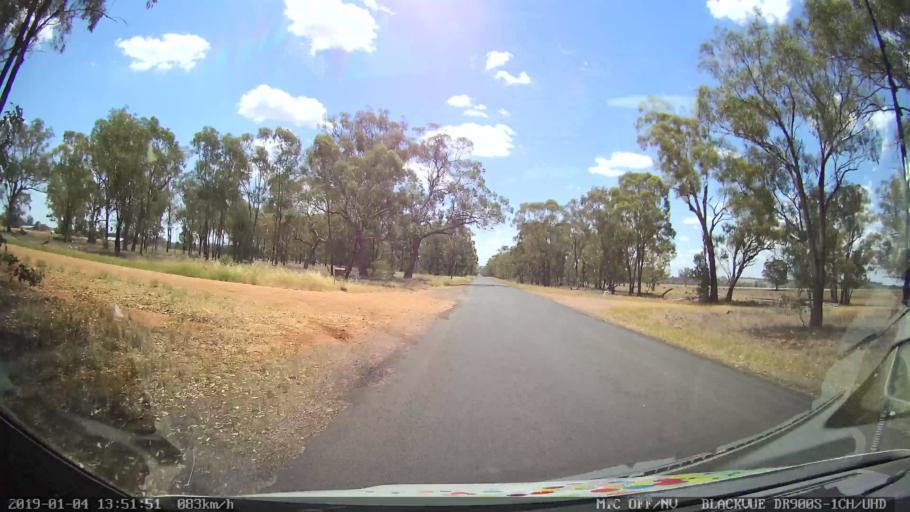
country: AU
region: New South Wales
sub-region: Dubbo Municipality
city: Dubbo
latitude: -32.4017
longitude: 148.5712
